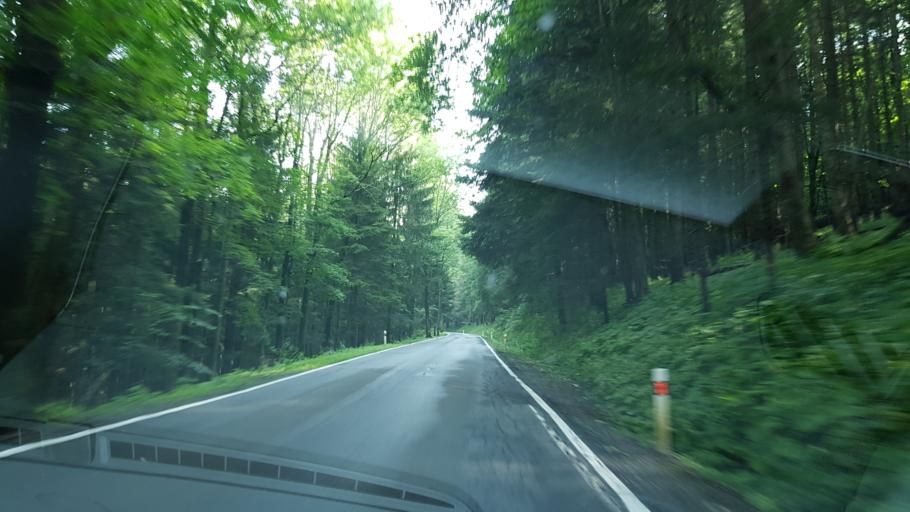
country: CZ
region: Olomoucky
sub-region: Okres Jesenik
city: Jesenik
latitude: 50.2129
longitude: 17.2478
